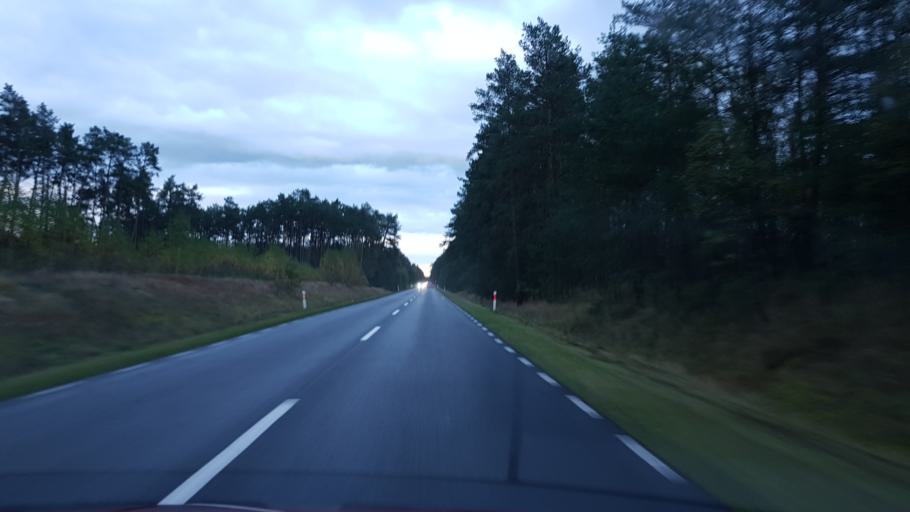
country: PL
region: Greater Poland Voivodeship
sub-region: Powiat pilski
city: Smilowo
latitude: 53.2067
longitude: 16.8472
